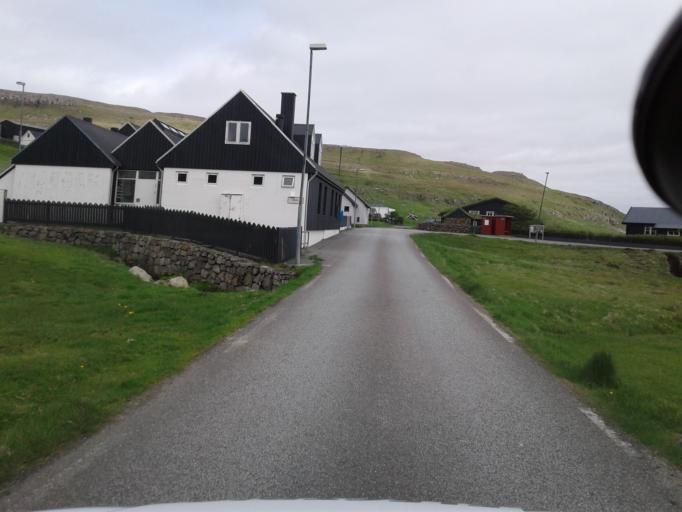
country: FO
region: Streymoy
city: Hoyvik
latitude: 62.0591
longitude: -6.8315
